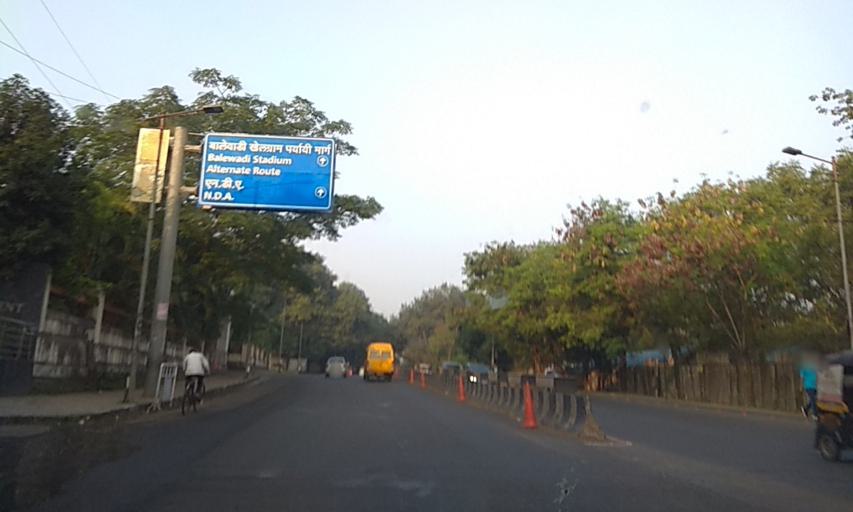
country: IN
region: Maharashtra
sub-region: Pune Division
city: Shivaji Nagar
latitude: 18.5418
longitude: 73.8267
